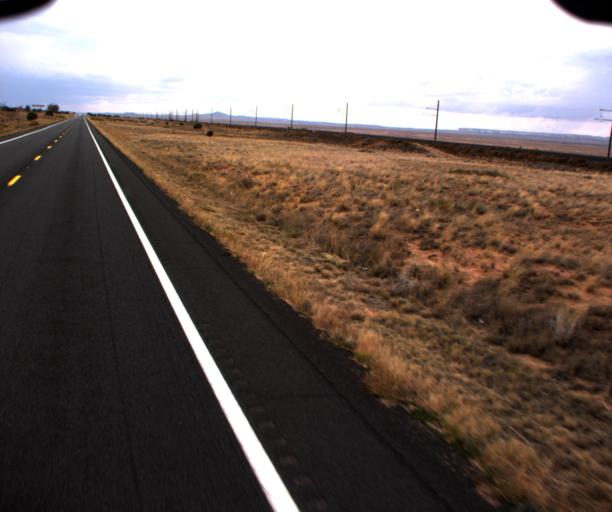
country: US
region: Arizona
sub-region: Coconino County
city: Kaibito
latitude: 36.4157
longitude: -110.8144
